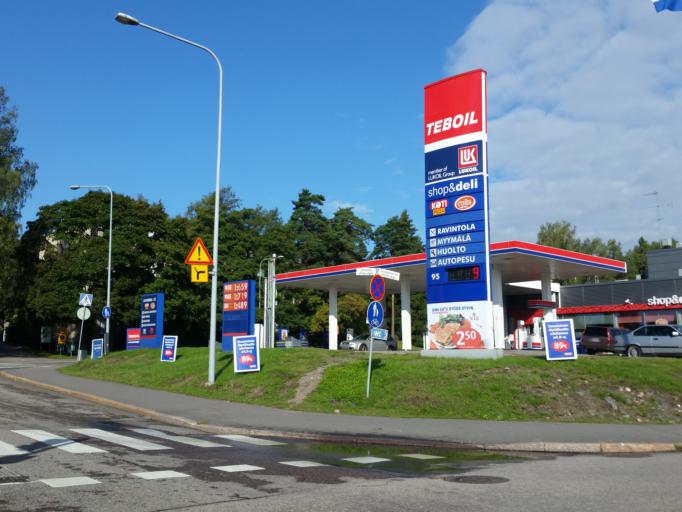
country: FI
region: Uusimaa
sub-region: Helsinki
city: Teekkarikylae
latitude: 60.2066
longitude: 24.8797
